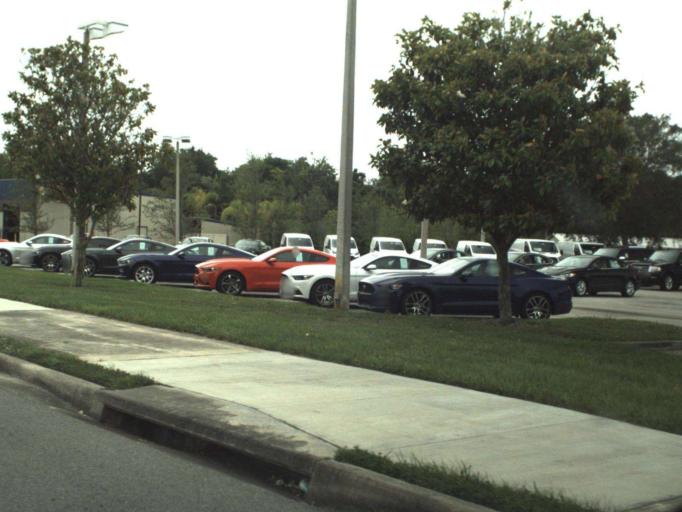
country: US
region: Florida
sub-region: Brevard County
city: Titusville
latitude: 28.5566
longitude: -80.8444
